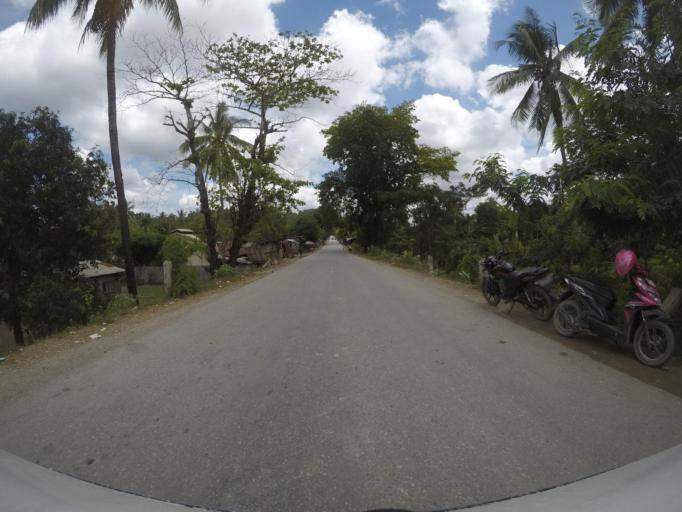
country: TL
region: Viqueque
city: Viqueque
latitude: -8.8679
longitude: 126.3690
